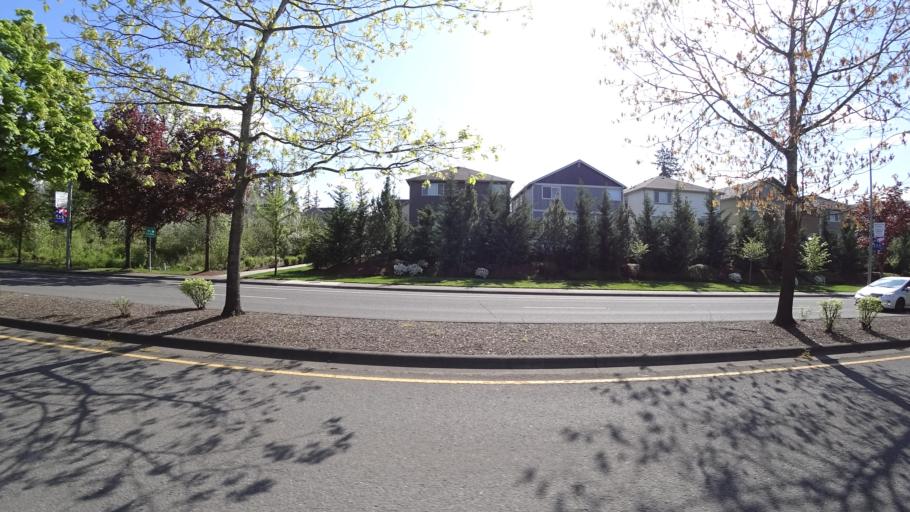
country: US
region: Oregon
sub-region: Washington County
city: Beaverton
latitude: 45.4466
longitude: -122.8261
